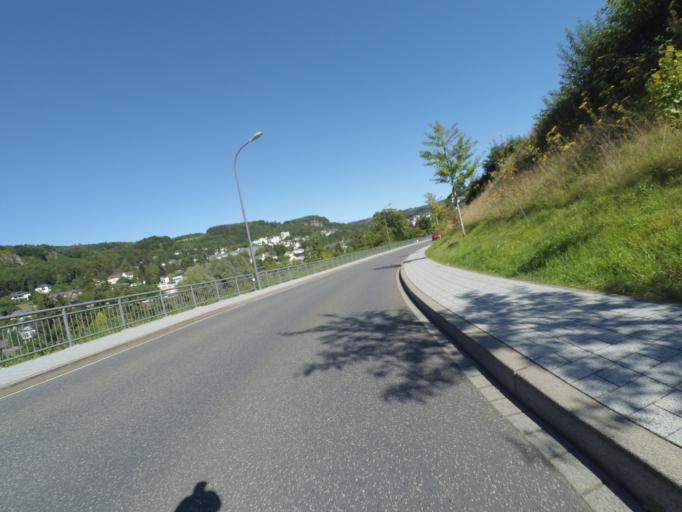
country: DE
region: Rheinland-Pfalz
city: Gerolstein
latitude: 50.2219
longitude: 6.6548
